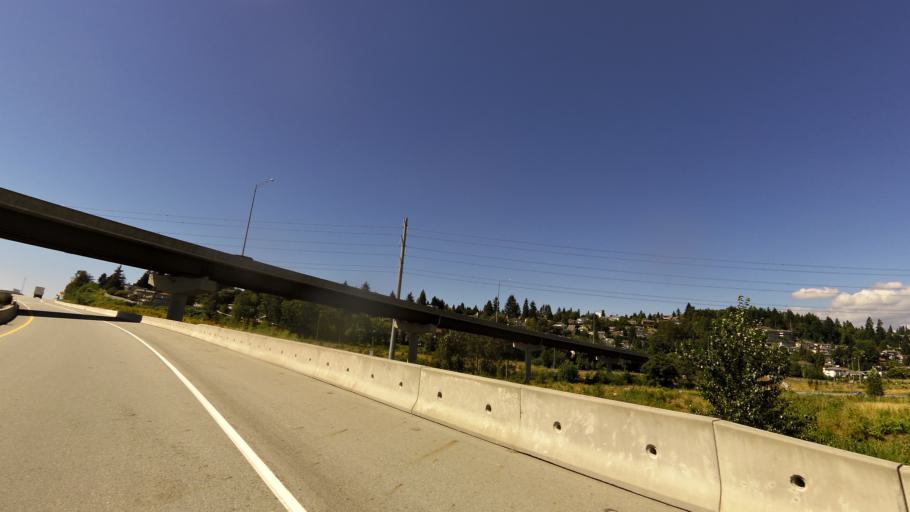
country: CA
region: British Columbia
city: Port Moody
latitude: 49.2297
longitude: -122.8299
